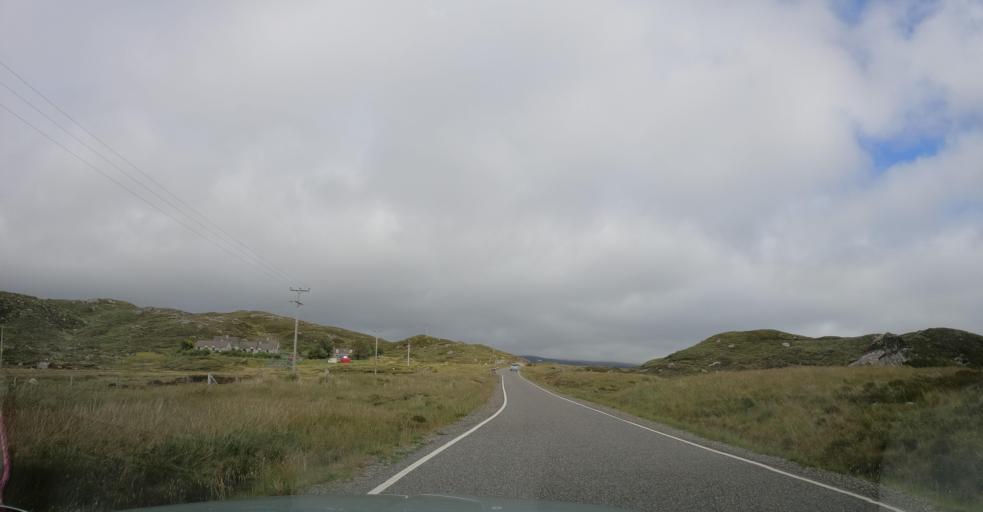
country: GB
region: Scotland
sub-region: Eilean Siar
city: Harris
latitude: 57.8881
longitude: -6.8090
